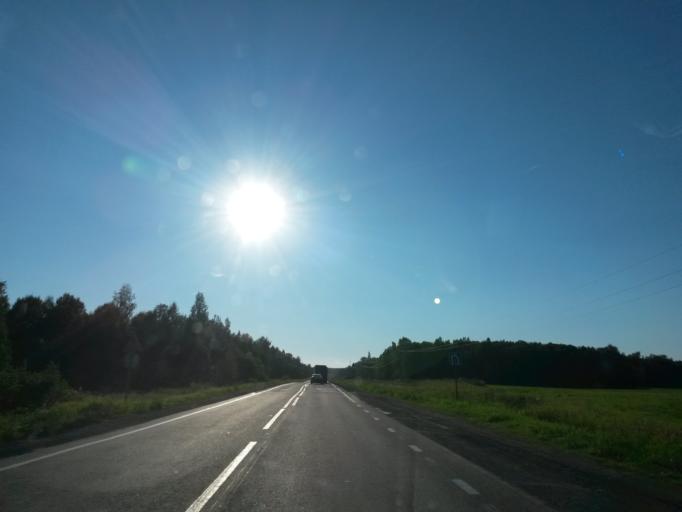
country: RU
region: Jaroslavl
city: Gavrilov-Yam
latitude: 57.2638
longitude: 40.0213
